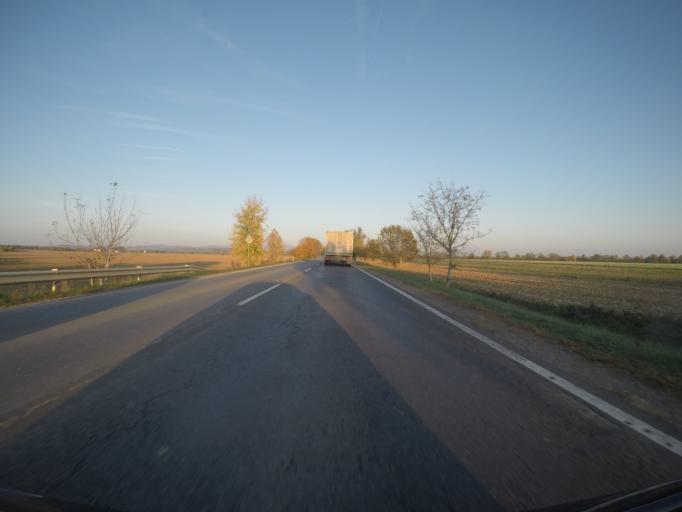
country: HU
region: Baranya
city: Szentlorinc
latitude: 46.0396
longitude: 17.9616
